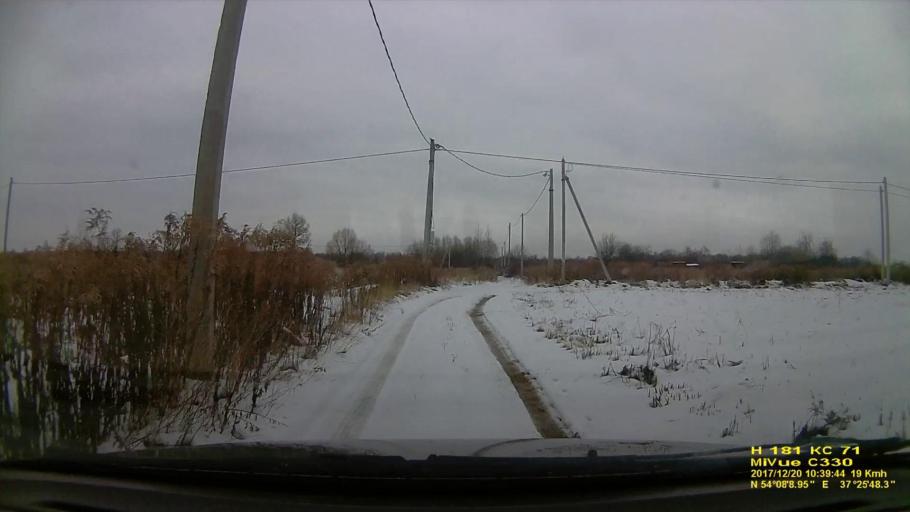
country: RU
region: Tula
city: Kosaya Gora
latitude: 54.1358
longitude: 37.4301
